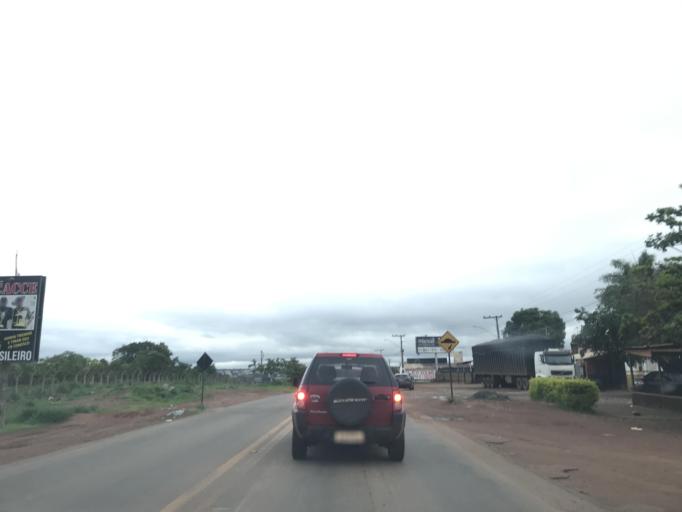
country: BR
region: Goias
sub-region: Luziania
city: Luziania
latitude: -16.2635
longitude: -47.9640
